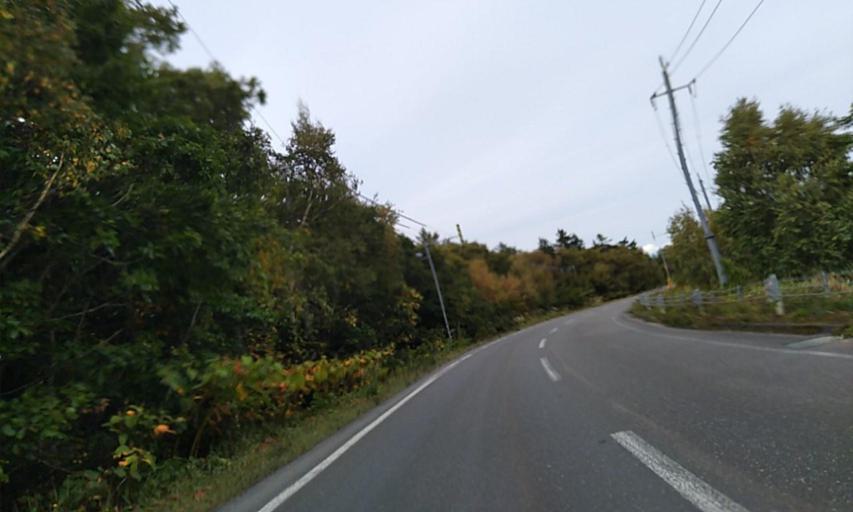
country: JP
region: Hokkaido
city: Makubetsu
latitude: 45.0002
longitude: 141.6966
